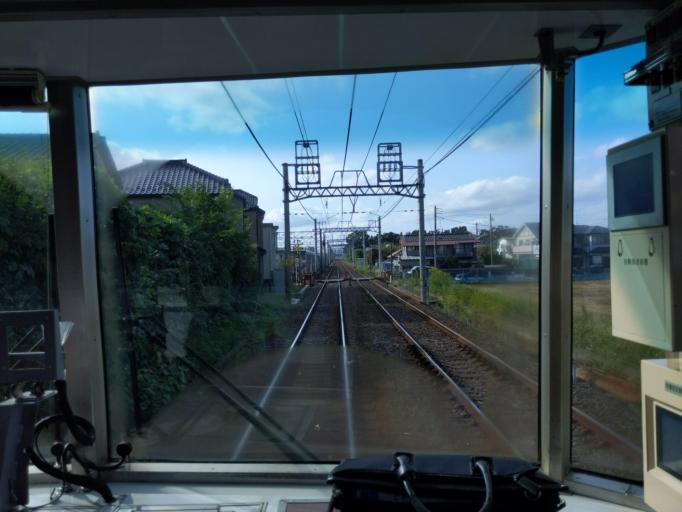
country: JP
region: Chiba
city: Kashiwa
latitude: 35.7766
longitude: 139.9843
